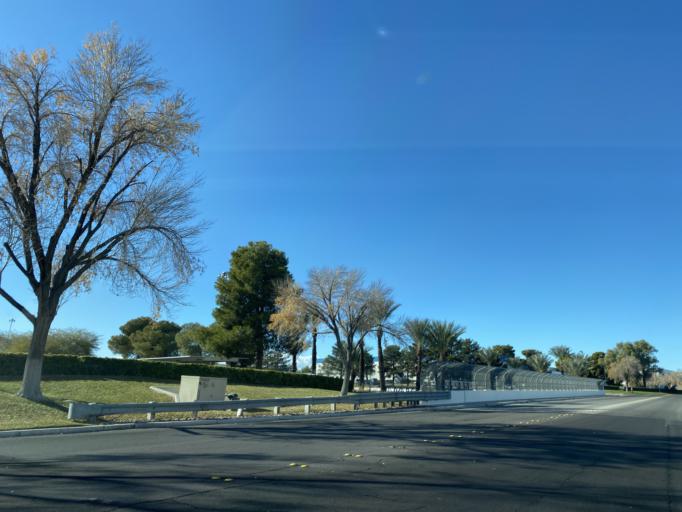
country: US
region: Nevada
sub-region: Clark County
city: Paradise
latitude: 36.0701
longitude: -115.1458
